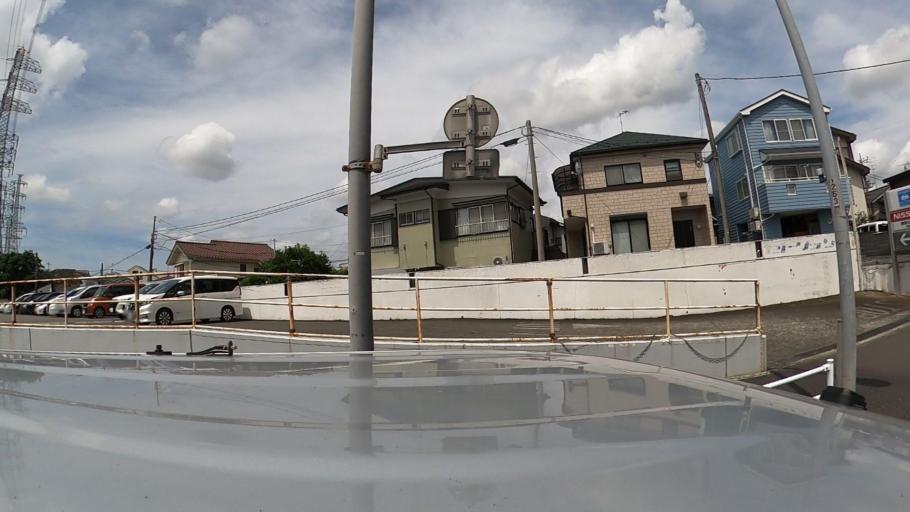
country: JP
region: Kanagawa
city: Fujisawa
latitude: 35.4131
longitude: 139.4697
